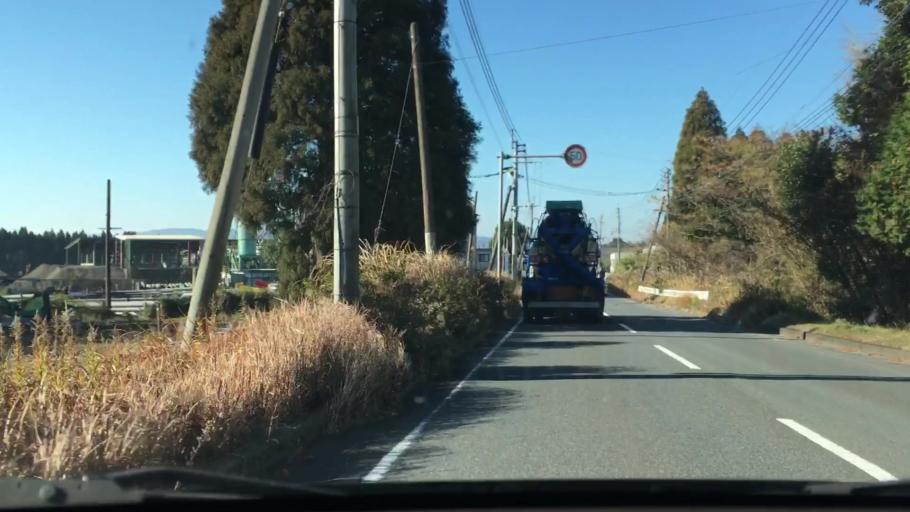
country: JP
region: Kagoshima
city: Kajiki
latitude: 31.7721
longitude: 130.6968
